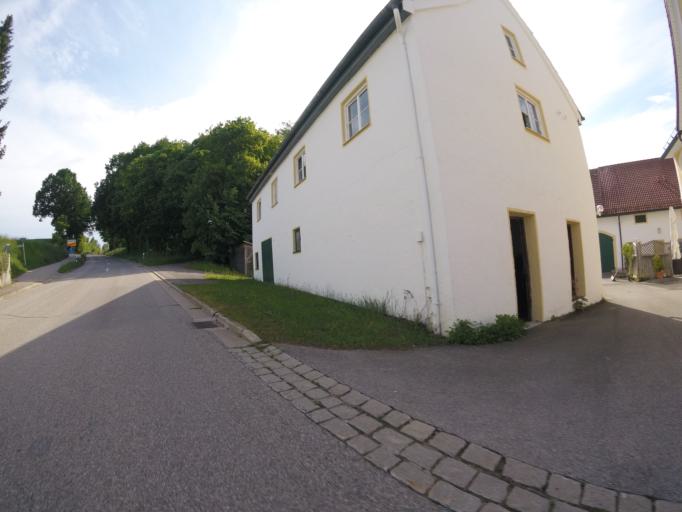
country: DE
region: Bavaria
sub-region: Upper Bavaria
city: Scheyern
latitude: 48.4615
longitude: 11.4488
